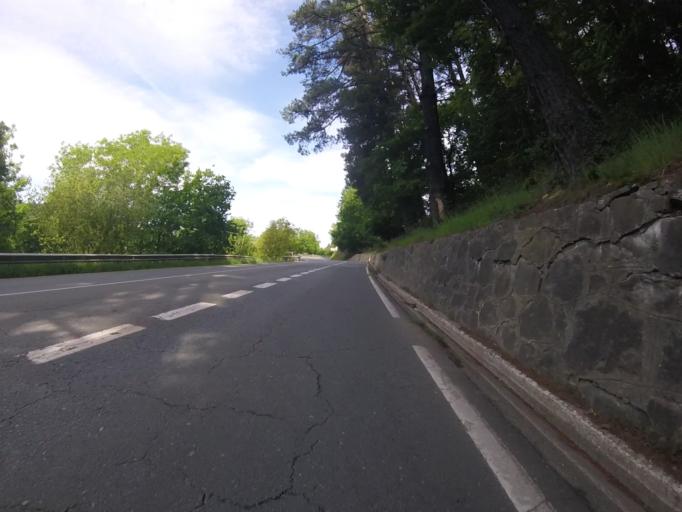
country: ES
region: Basque Country
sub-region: Provincia de Guipuzcoa
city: Zumarraga
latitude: 43.0823
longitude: -2.3007
